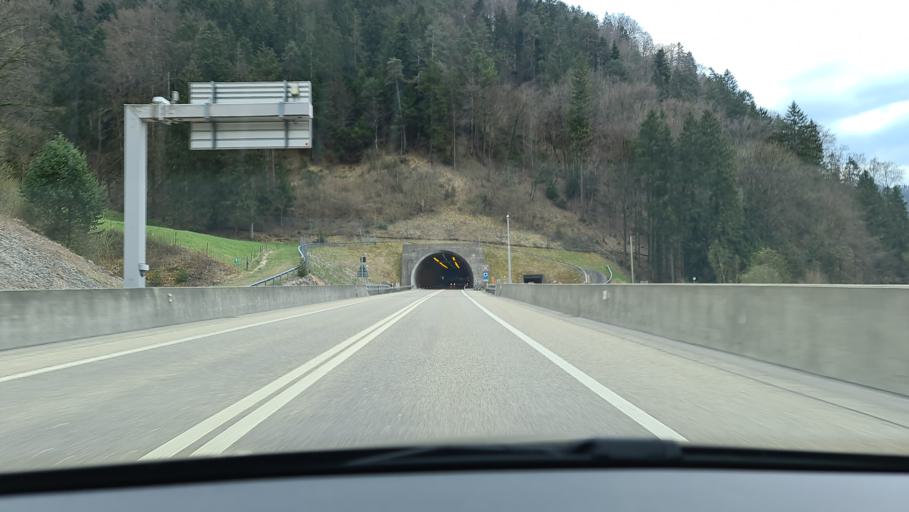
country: CH
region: Jura
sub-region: Delemont District
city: Courrendlin
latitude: 47.3108
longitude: 7.3925
